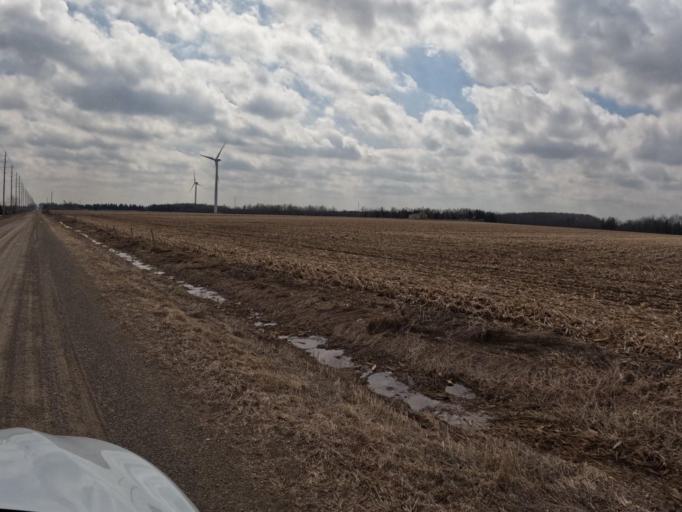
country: CA
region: Ontario
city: Shelburne
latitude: 44.0384
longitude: -80.3171
